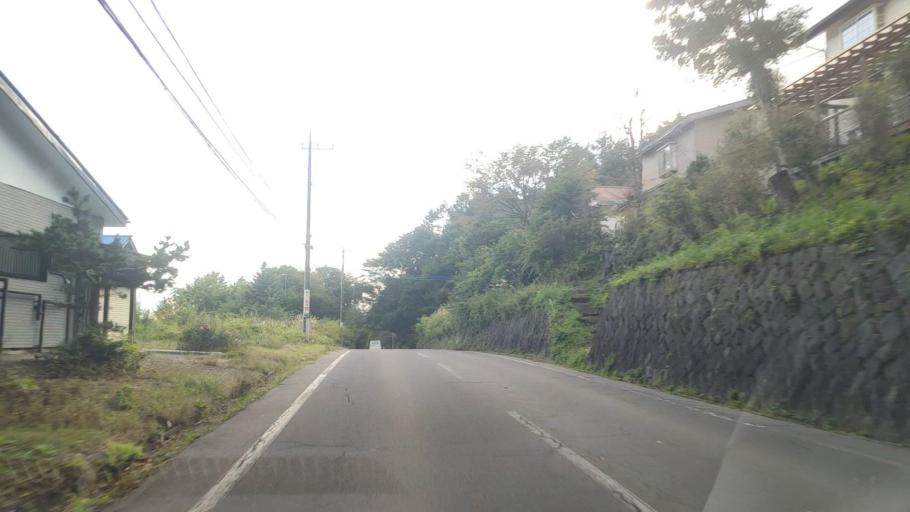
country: JP
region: Gunma
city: Nakanojomachi
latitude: 36.5903
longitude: 138.5770
